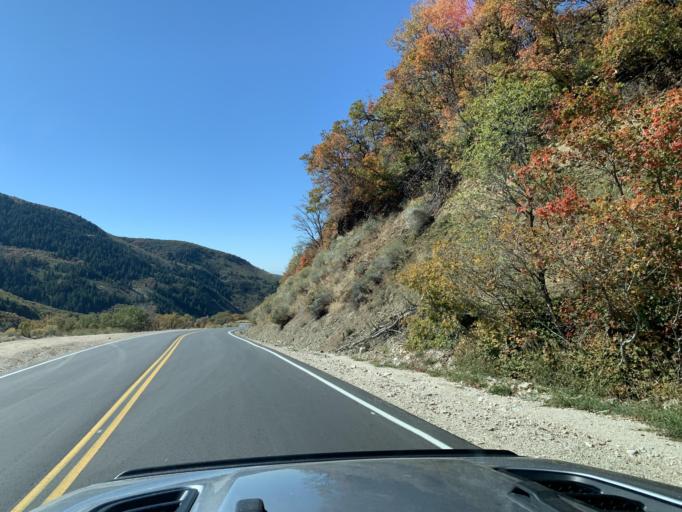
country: US
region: Utah
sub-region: Weber County
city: Liberty
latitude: 41.3198
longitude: -111.9041
